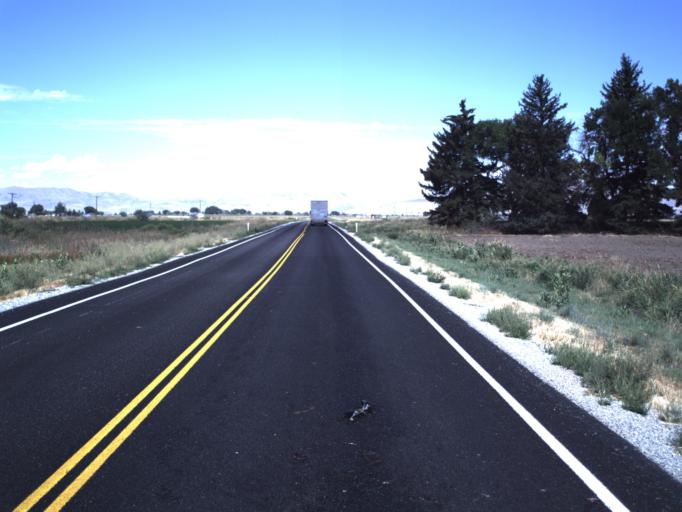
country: US
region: Utah
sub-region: Box Elder County
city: Elwood
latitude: 41.6473
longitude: -112.1347
